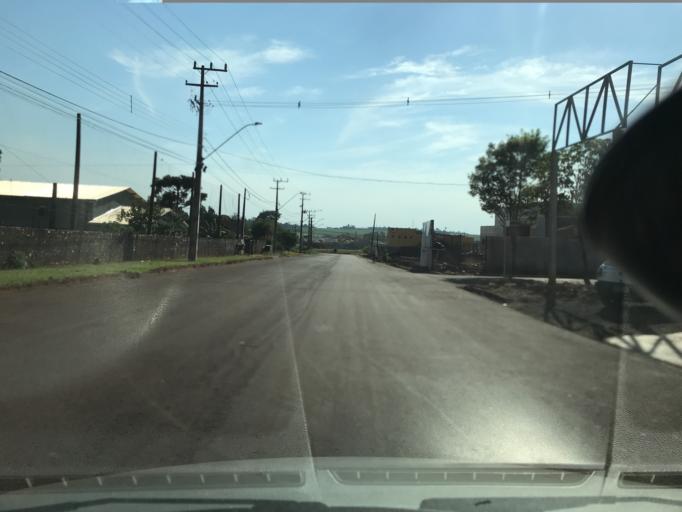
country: BR
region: Parana
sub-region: Palotina
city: Palotina
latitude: -24.2950
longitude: -53.8317
